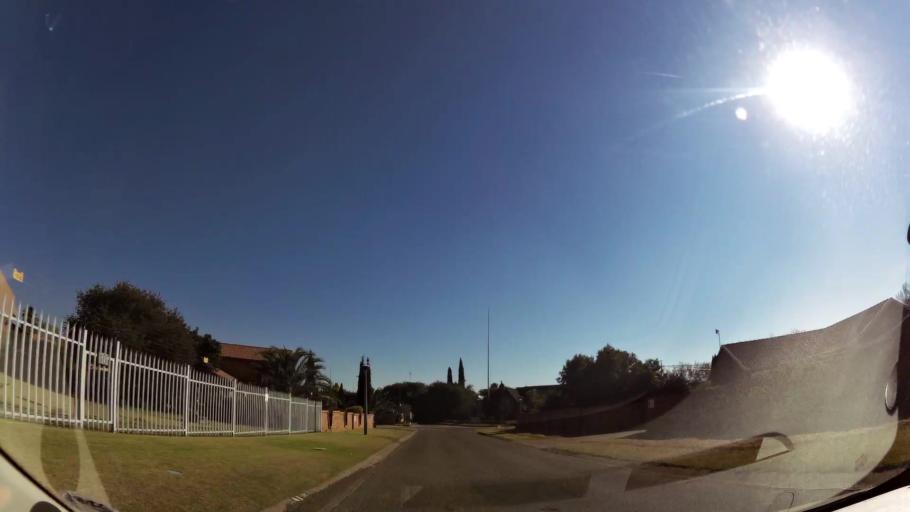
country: ZA
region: Mpumalanga
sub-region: Nkangala District Municipality
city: Witbank
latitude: -25.8861
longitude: 29.2545
